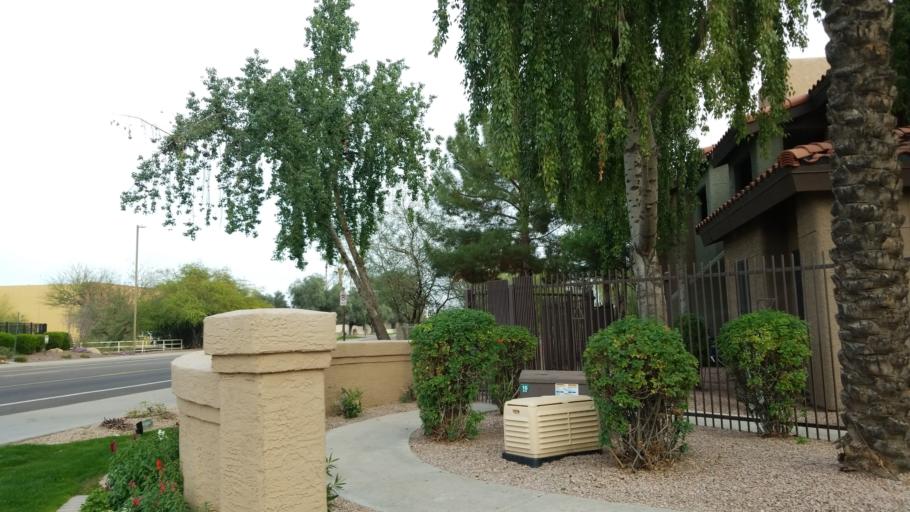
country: US
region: Arizona
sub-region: Maricopa County
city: Paradise Valley
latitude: 33.5783
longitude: -111.9289
